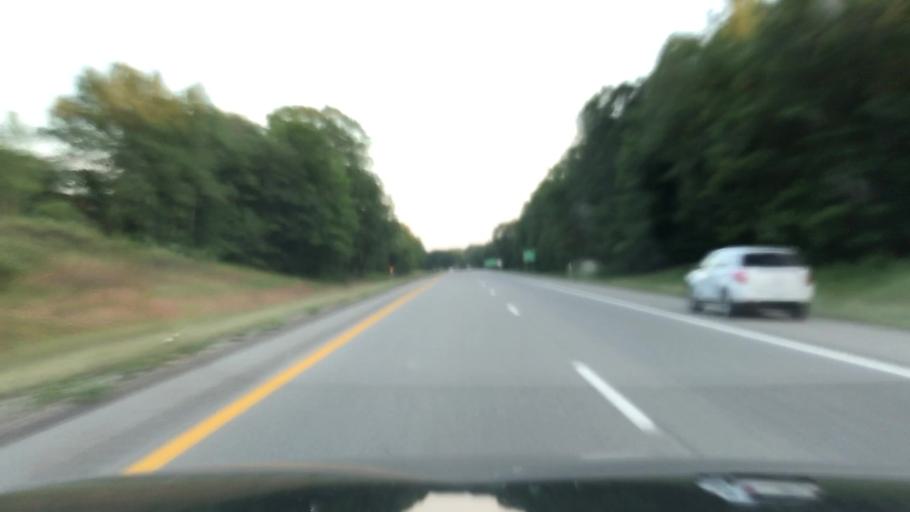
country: US
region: Michigan
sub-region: Montcalm County
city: Howard City
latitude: 43.5006
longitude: -85.4867
